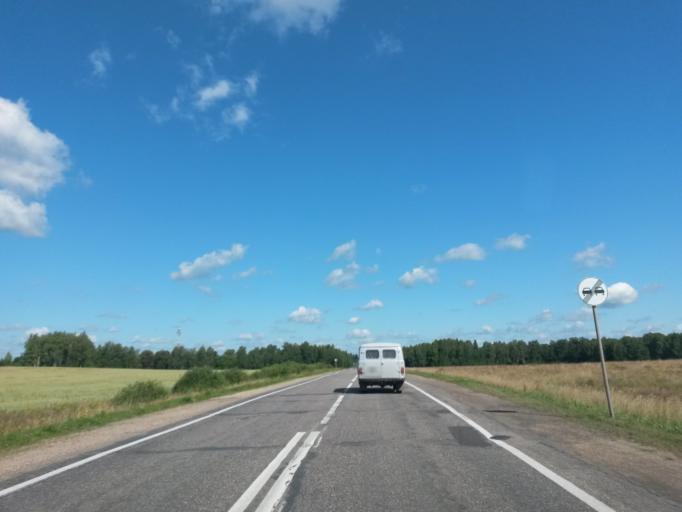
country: RU
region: Jaroslavl
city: Gavrilov-Yam
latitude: 57.4030
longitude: 39.9213
